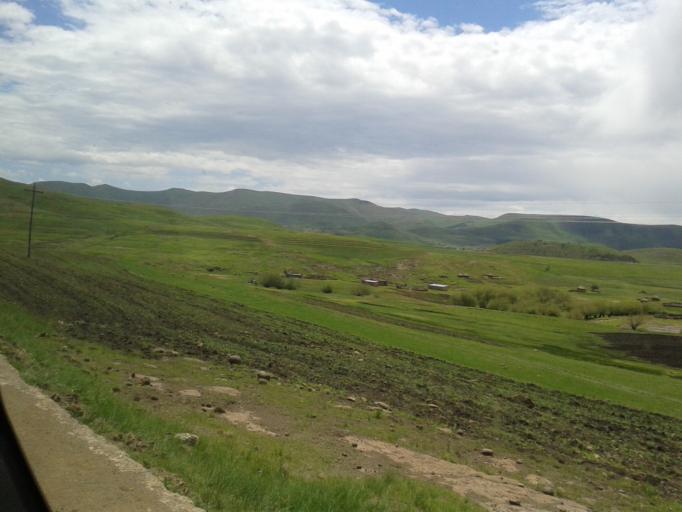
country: LS
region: Maseru
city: Nako
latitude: -29.8626
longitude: 28.0383
